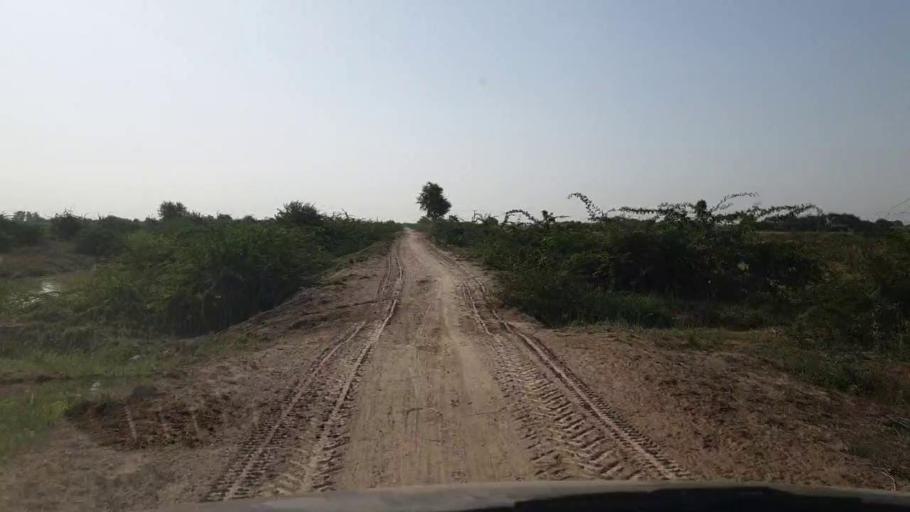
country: PK
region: Sindh
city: Kadhan
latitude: 24.5962
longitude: 69.0755
